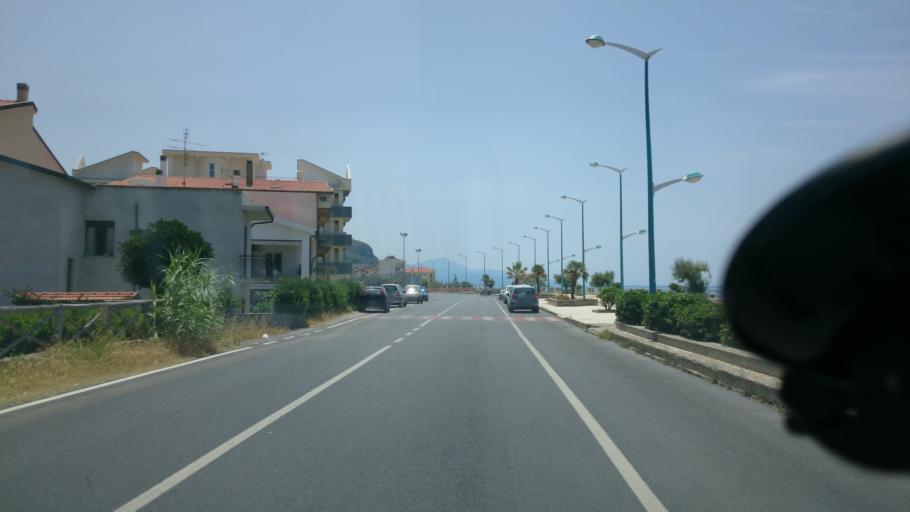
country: IT
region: Calabria
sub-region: Provincia di Cosenza
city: Cetraro Marina
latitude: 39.5162
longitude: 15.9344
